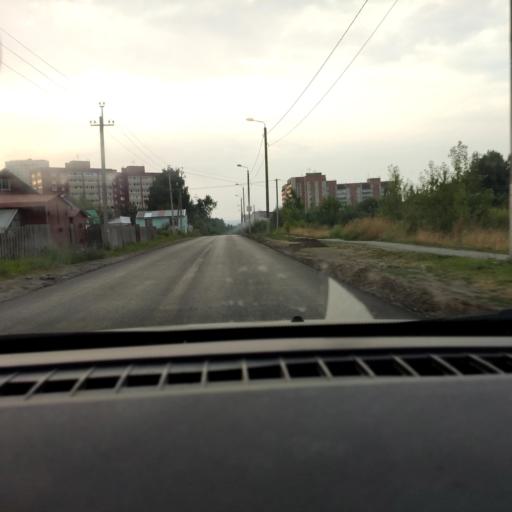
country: RU
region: Perm
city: Perm
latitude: 58.1030
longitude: 56.2902
